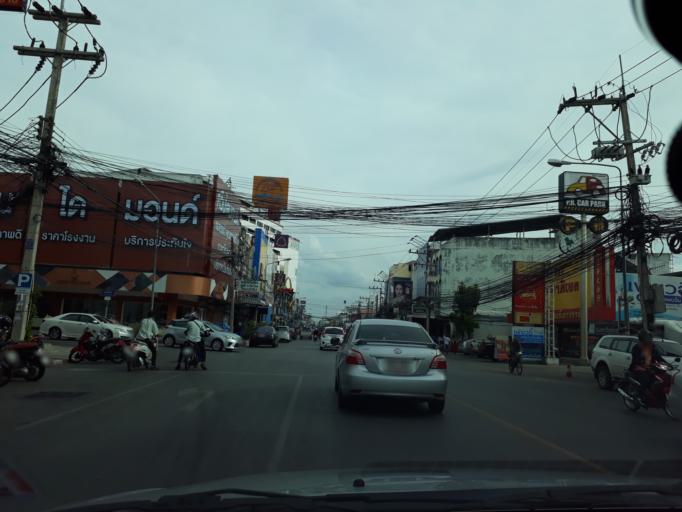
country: TH
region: Khon Kaen
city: Khon Kaen
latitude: 16.4250
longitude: 102.8333
